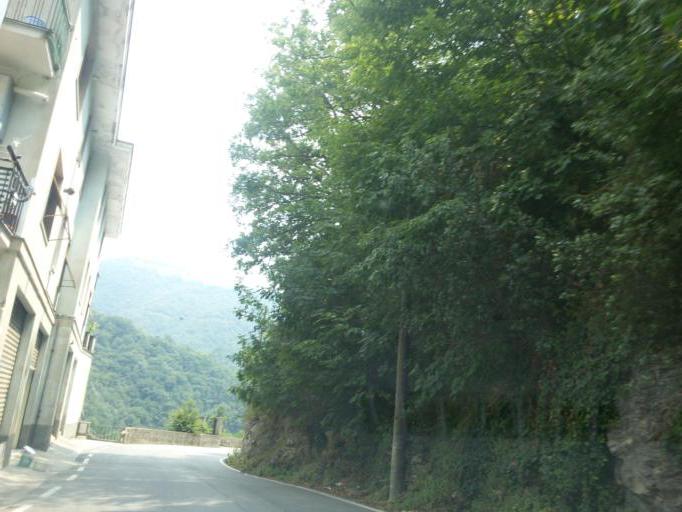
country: IT
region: Liguria
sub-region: Provincia di Genova
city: Piccarello
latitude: 44.4192
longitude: 9.0009
